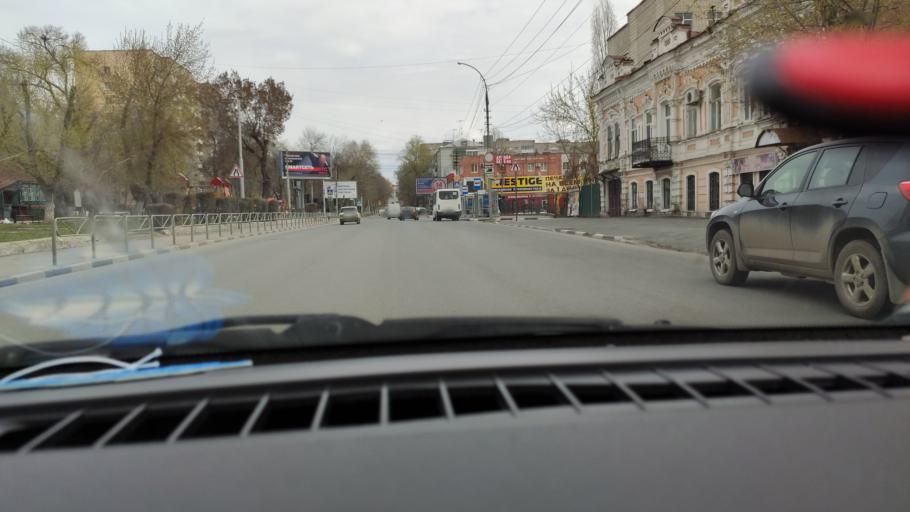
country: RU
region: Saratov
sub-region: Saratovskiy Rayon
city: Saratov
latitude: 51.5391
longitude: 46.0445
